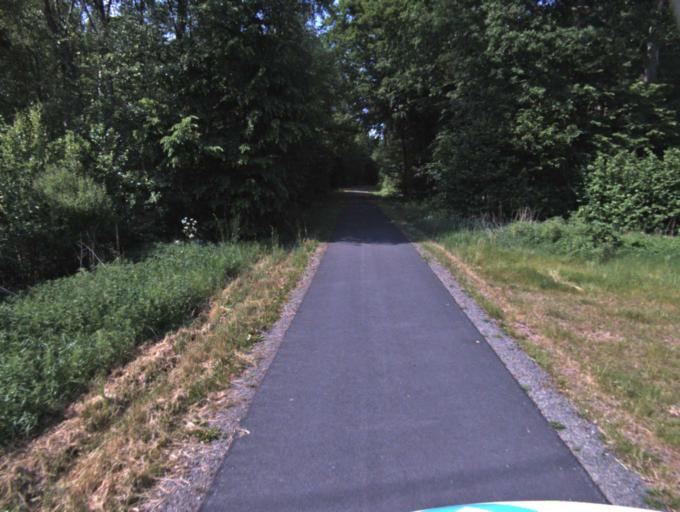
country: SE
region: Skane
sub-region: Kristianstads Kommun
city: Tollarp
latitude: 56.1806
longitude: 14.2846
